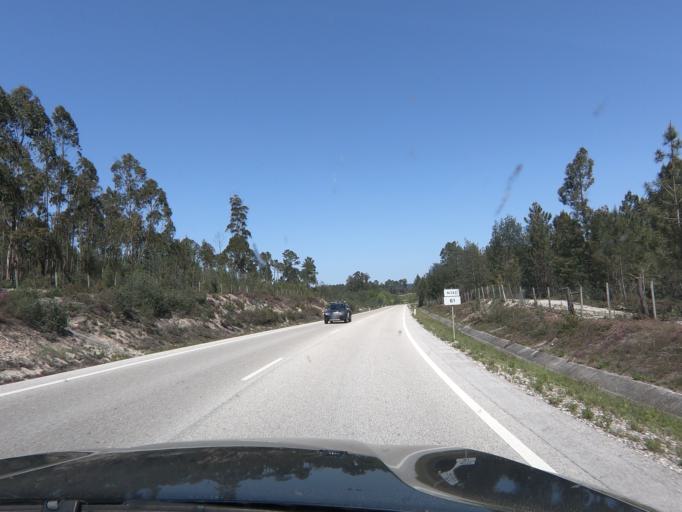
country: PT
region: Coimbra
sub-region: Lousa
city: Lousa
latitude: 40.1235
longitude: -8.2808
